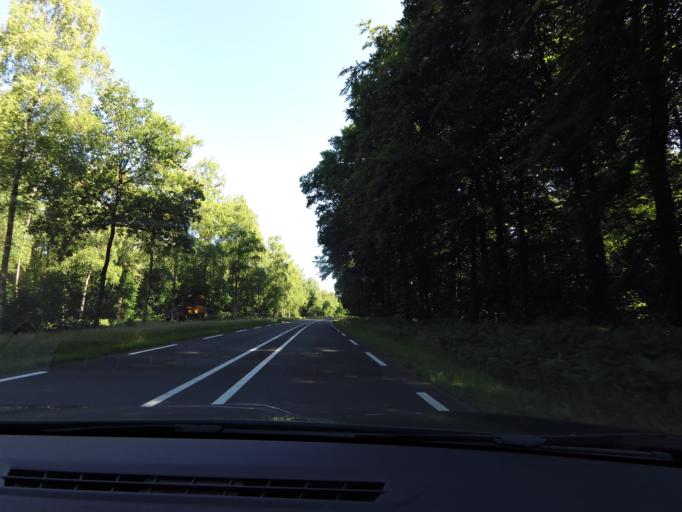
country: NL
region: Overijssel
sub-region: Gemeente Twenterand
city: Den Ham
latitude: 52.4720
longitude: 6.4273
